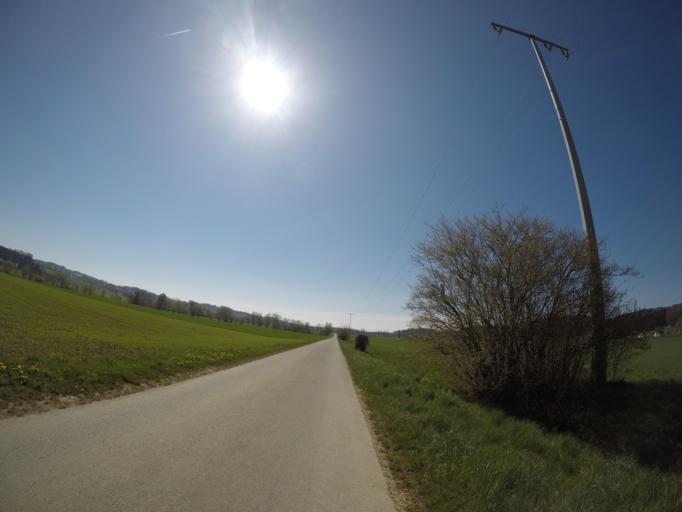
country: DE
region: Baden-Wuerttemberg
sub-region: Tuebingen Region
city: Wilhelmsdorf
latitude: 47.8405
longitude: 9.4436
